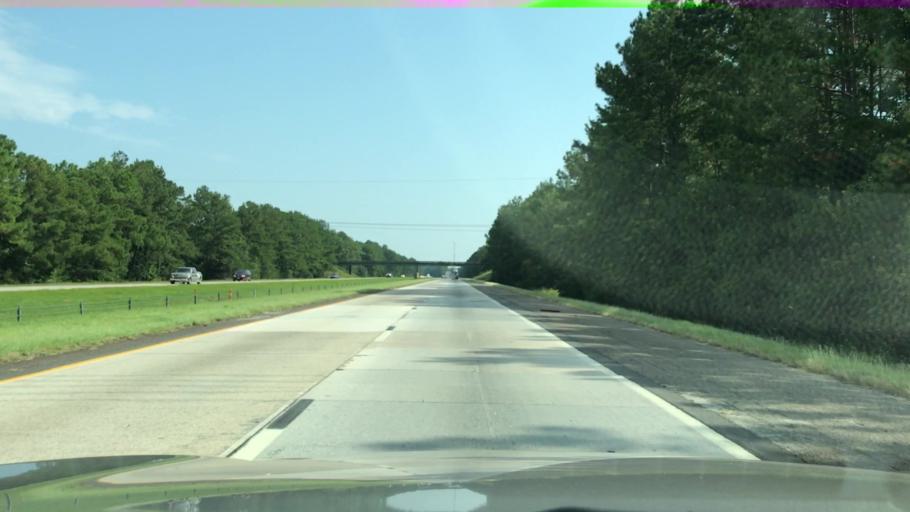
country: US
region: South Carolina
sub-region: Hampton County
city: Yemassee
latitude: 32.7799
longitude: -80.7916
